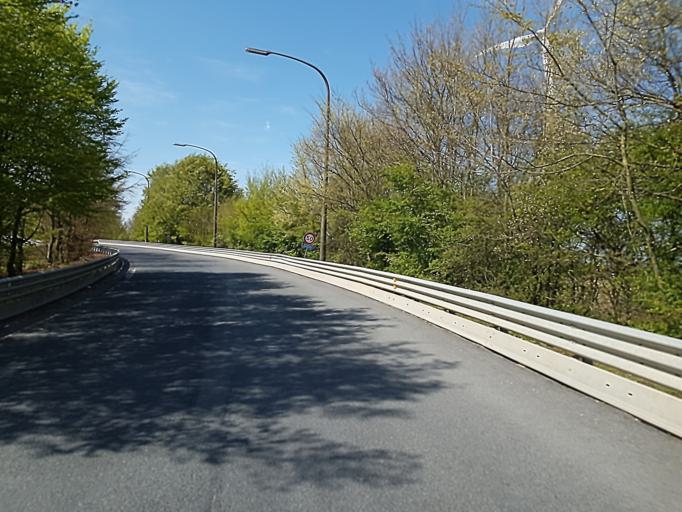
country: FR
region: Nord-Pas-de-Calais
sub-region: Departement du Nord
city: Camphin-en-Pevele
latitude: 50.6111
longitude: 3.3017
